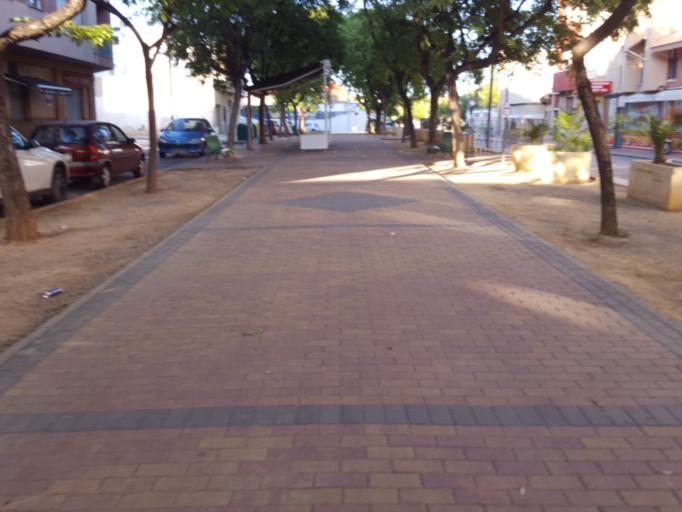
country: ES
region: Murcia
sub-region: Murcia
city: Murcia
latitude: 37.9973
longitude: -1.1746
